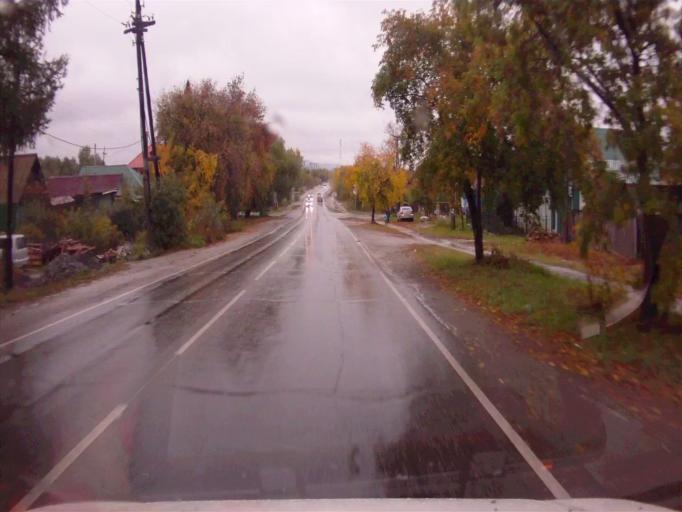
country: RU
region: Chelyabinsk
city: Kyshtym
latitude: 55.7087
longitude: 60.5571
